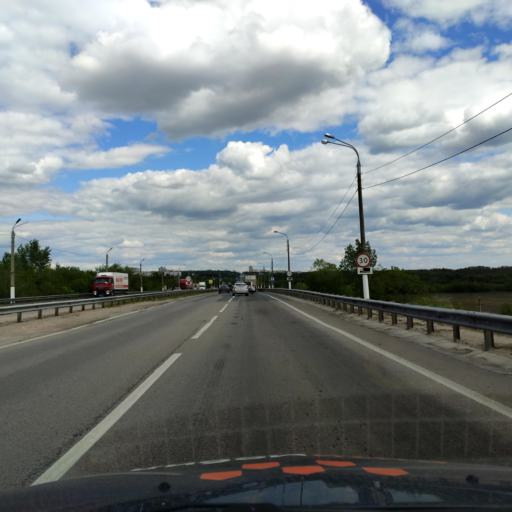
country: RU
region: Voronezj
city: Pridonskoy
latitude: 51.6512
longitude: 39.0713
